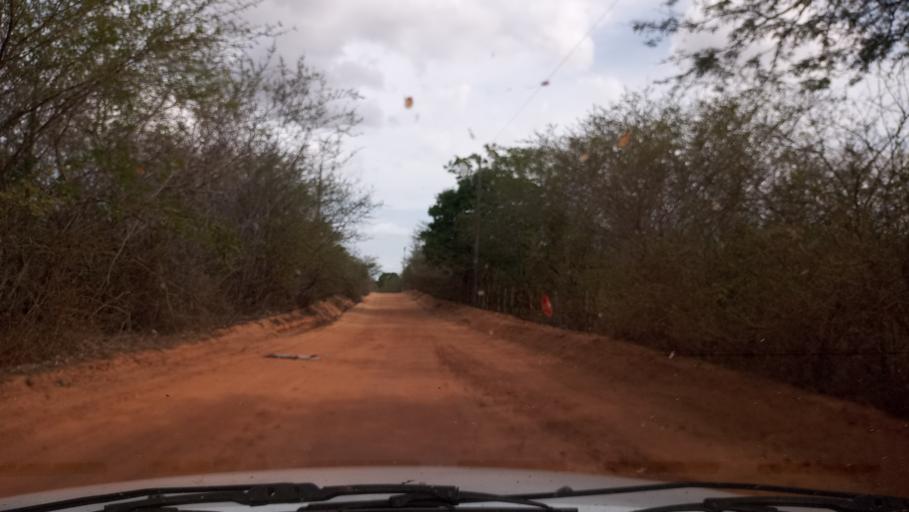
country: BR
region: Rio Grande do Norte
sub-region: Joao Camara
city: Joao Camara
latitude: -5.5026
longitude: -35.8248
